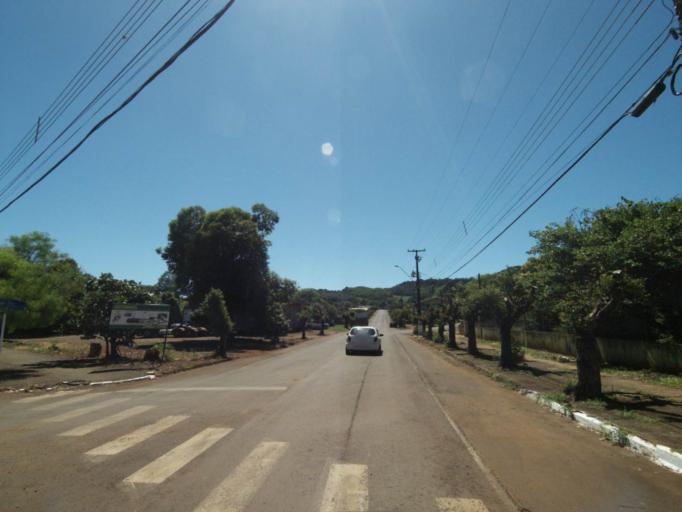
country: BR
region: Parana
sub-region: Pato Branco
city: Pato Branco
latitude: -26.2643
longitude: -52.7797
